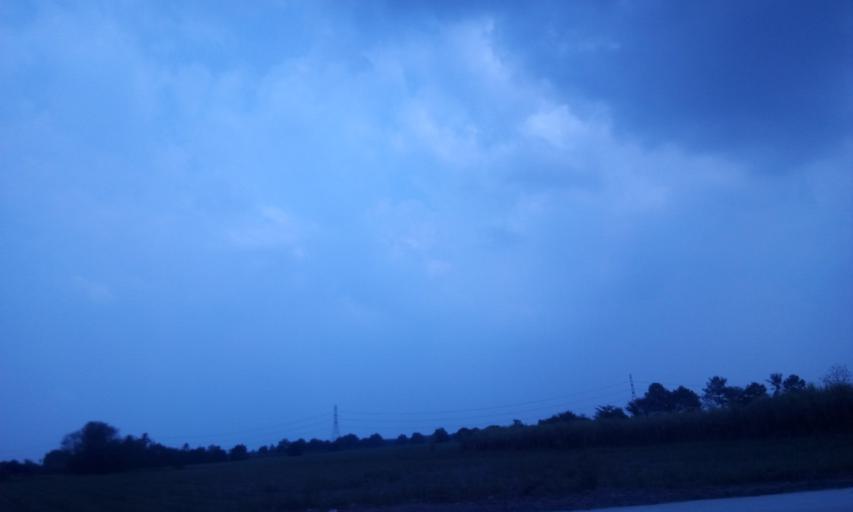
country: TH
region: Chon Buri
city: Ban Bueng
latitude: 13.2993
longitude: 101.1781
